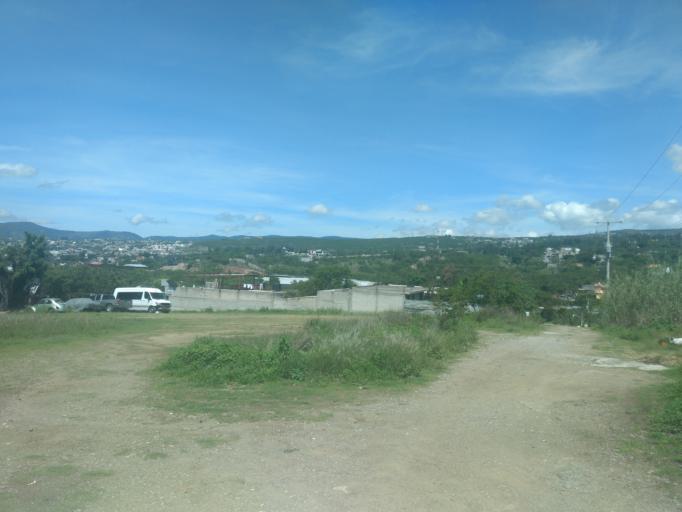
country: MX
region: Oaxaca
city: Ciudad de Huajuapam de Leon
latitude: 17.8242
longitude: -97.7844
